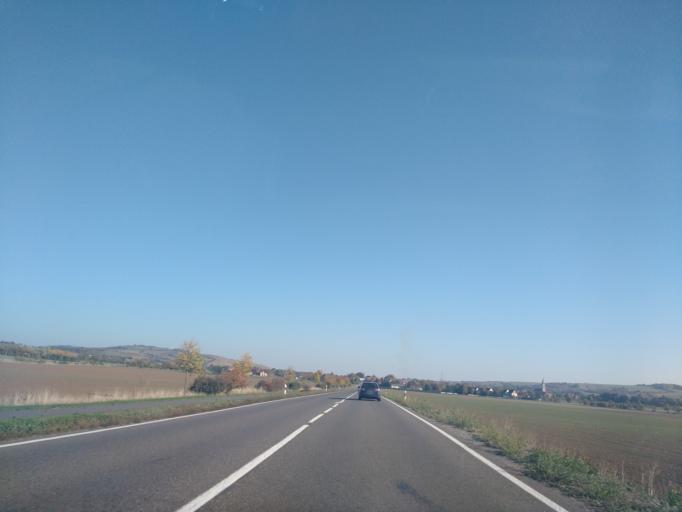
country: DE
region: Saxony-Anhalt
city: Bennungen
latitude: 51.4645
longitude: 11.1010
